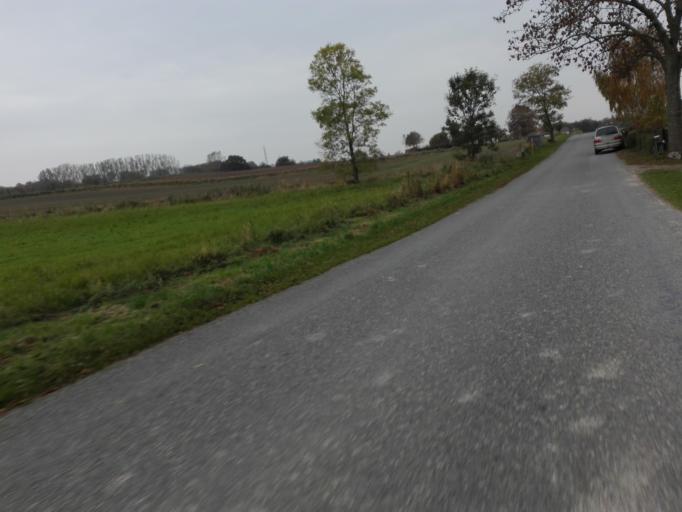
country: DK
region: Central Jutland
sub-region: Arhus Kommune
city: Beder
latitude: 56.0484
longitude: 10.2230
